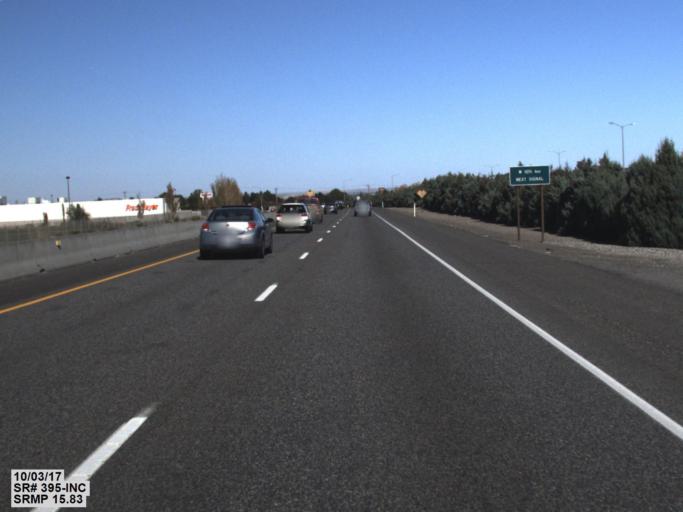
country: US
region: Washington
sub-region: Benton County
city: Kennewick
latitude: 46.1946
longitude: -119.1631
